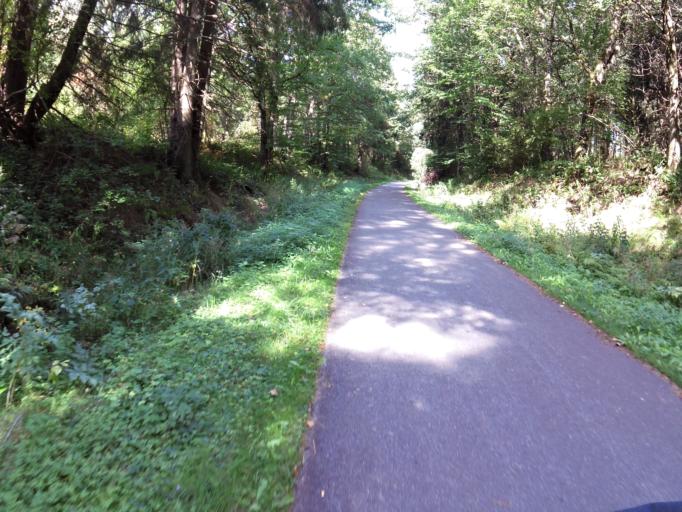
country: DE
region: Rheinland-Pfalz
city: Arzfeld
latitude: 50.0974
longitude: 6.2705
